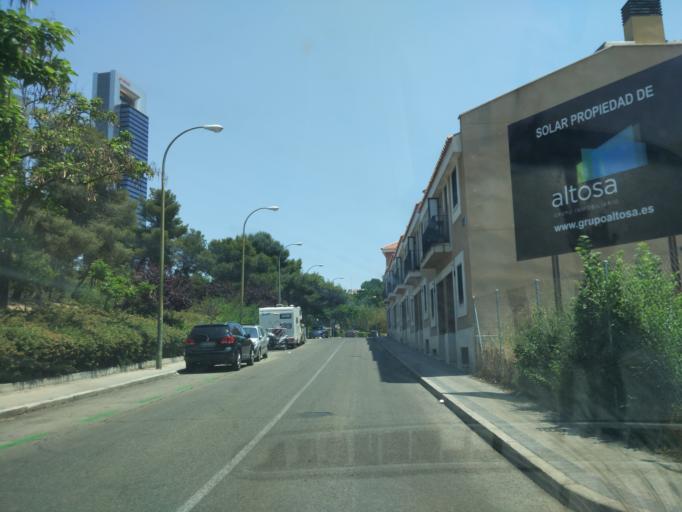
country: ES
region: Madrid
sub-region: Provincia de Madrid
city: Chamartin
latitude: 40.4735
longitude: -3.6946
